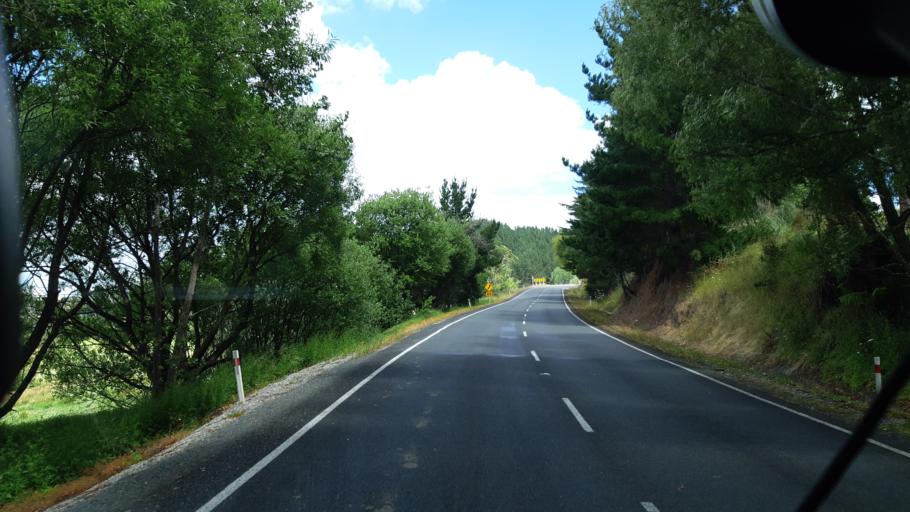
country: NZ
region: Northland
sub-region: Far North District
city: Taipa
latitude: -35.2544
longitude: 173.5549
